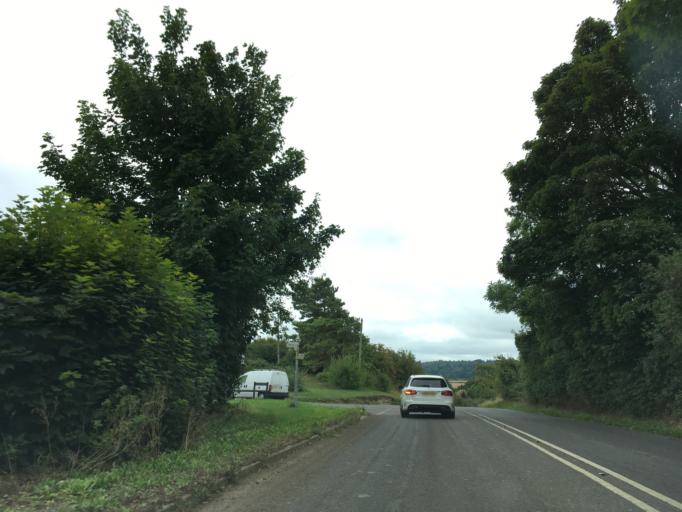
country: GB
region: England
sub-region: Bath and North East Somerset
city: Keynsham
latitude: 51.3911
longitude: -2.4847
